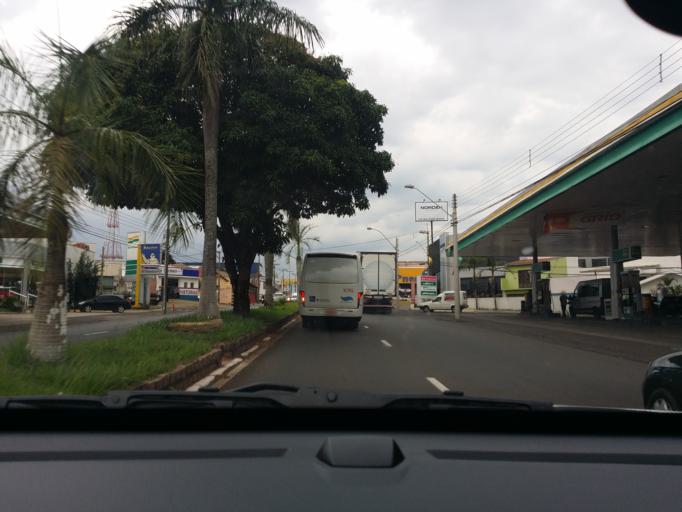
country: BR
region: Sao Paulo
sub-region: Sao Carlos
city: Sao Carlos
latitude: -22.0330
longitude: -47.8848
